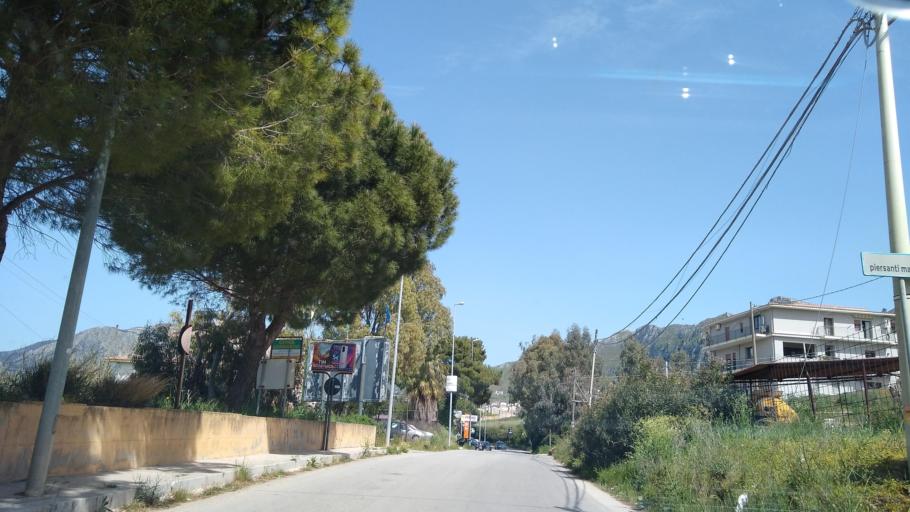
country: IT
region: Sicily
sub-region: Palermo
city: San Giuseppe Jato
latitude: 37.9751
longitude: 13.1962
